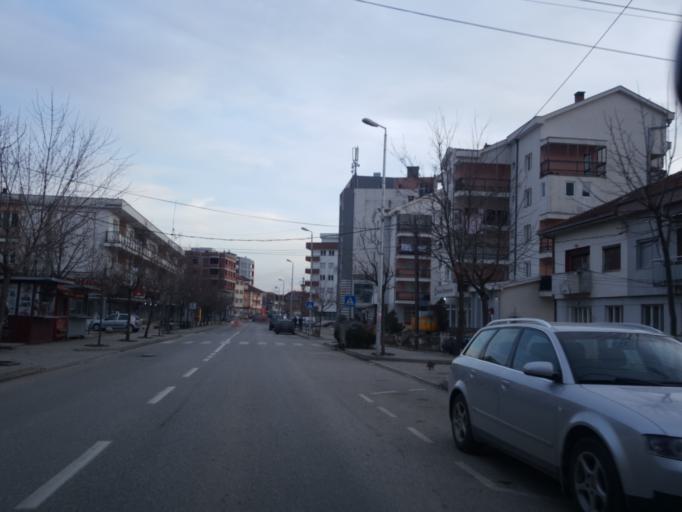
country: XK
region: Pec
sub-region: Komuna e Istogut
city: Istok
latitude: 42.7804
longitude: 20.4868
